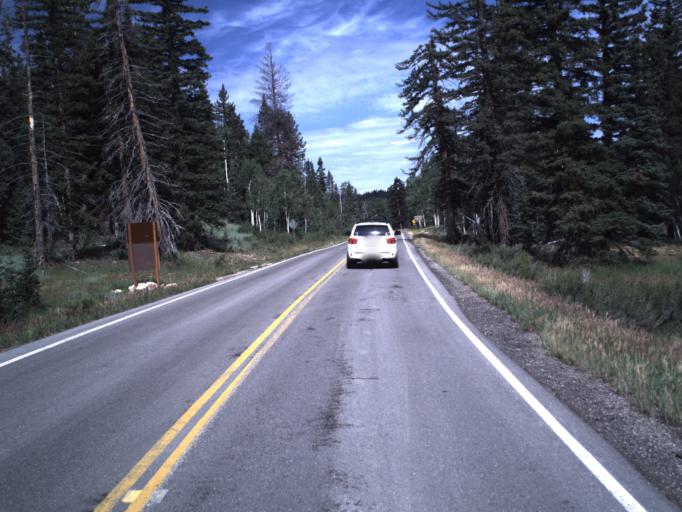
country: US
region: Utah
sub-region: Iron County
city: Parowan
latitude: 37.5140
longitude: -112.6896
